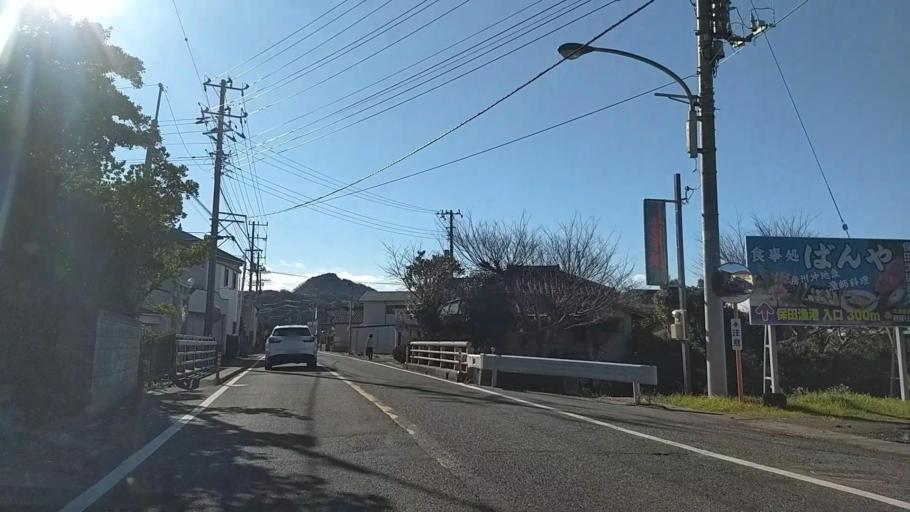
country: JP
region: Chiba
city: Tateyama
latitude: 35.1353
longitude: 139.8381
